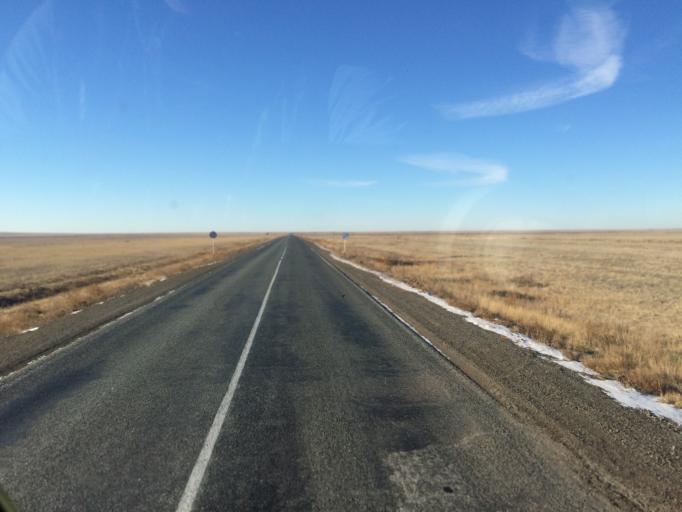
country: KZ
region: Aqtoebe
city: Khromtau
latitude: 50.1840
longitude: 58.6621
